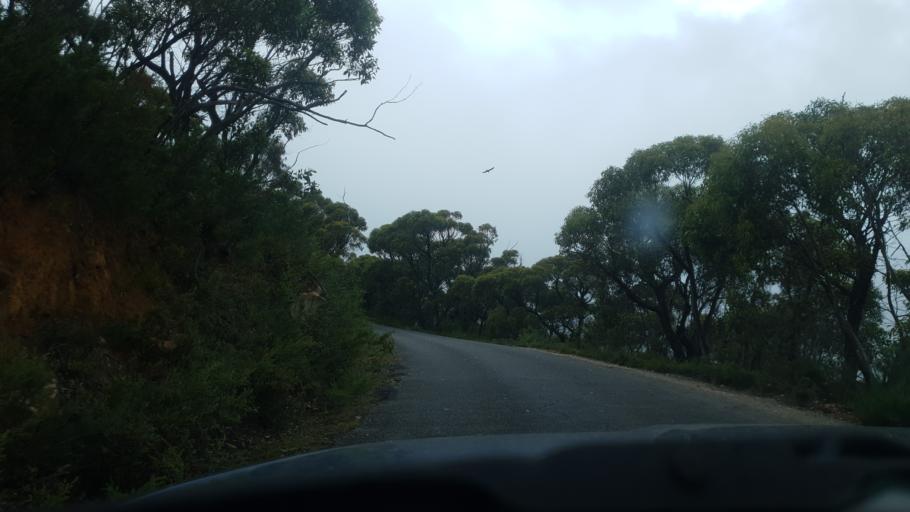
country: AU
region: Victoria
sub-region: Northern Grampians
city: Stawell
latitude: -37.2697
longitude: 142.5786
